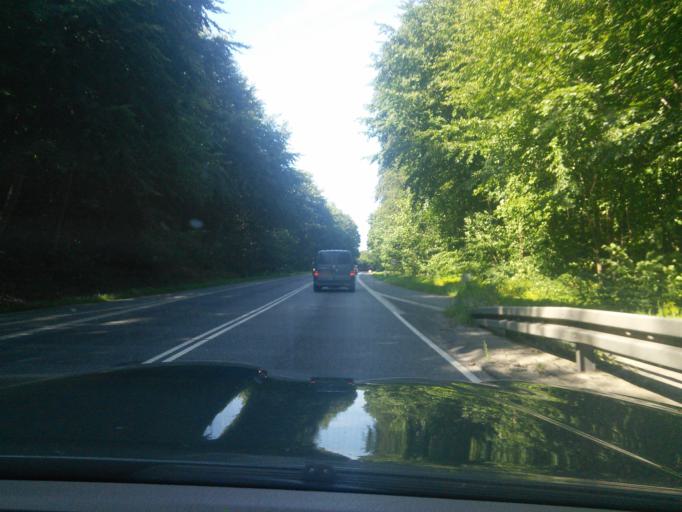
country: DK
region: Capital Region
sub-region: Halsnaes Kommune
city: Frederiksvaerk
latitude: 55.9755
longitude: 12.0291
